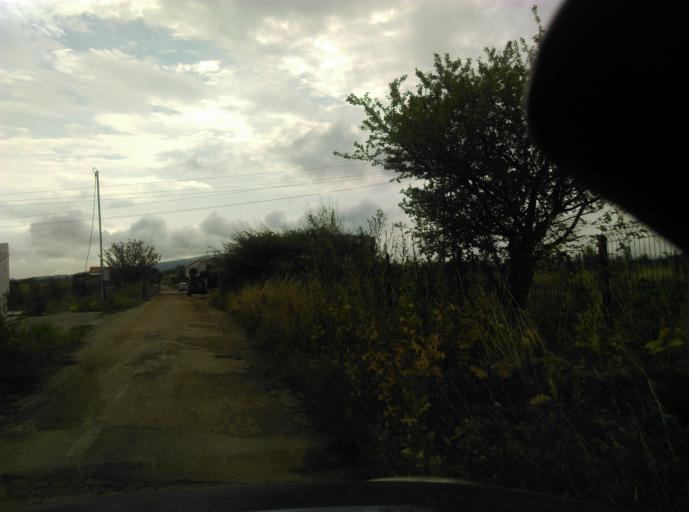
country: BG
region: Sofia-Capital
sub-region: Stolichna Obshtina
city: Sofia
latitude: 42.5917
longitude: 23.3730
